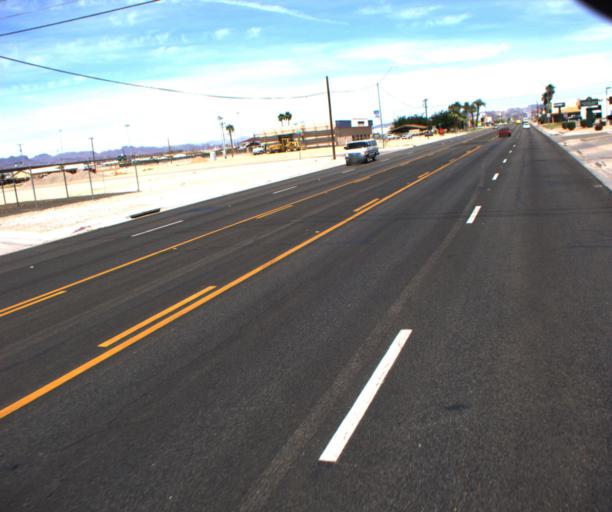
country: US
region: Arizona
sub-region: La Paz County
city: Parker
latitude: 34.1522
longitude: -114.2848
